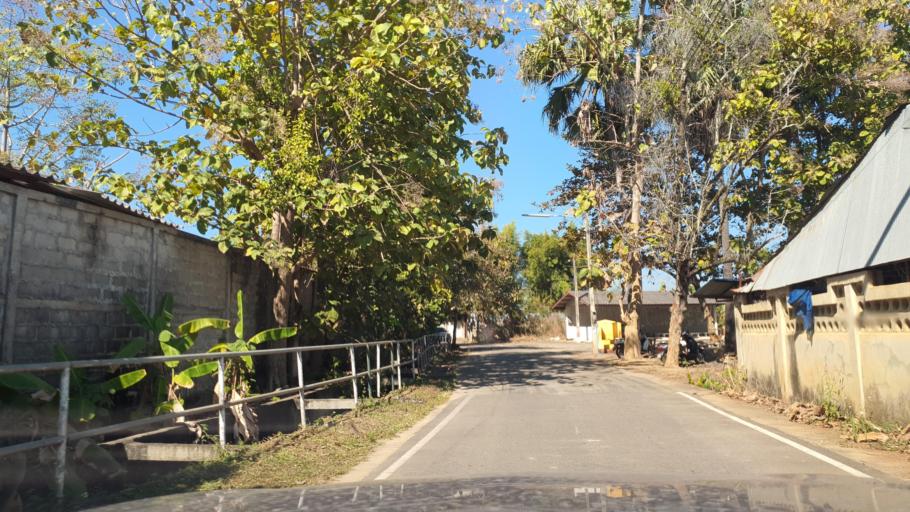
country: TH
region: Chiang Mai
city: Hang Dong
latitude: 18.6792
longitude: 98.9274
